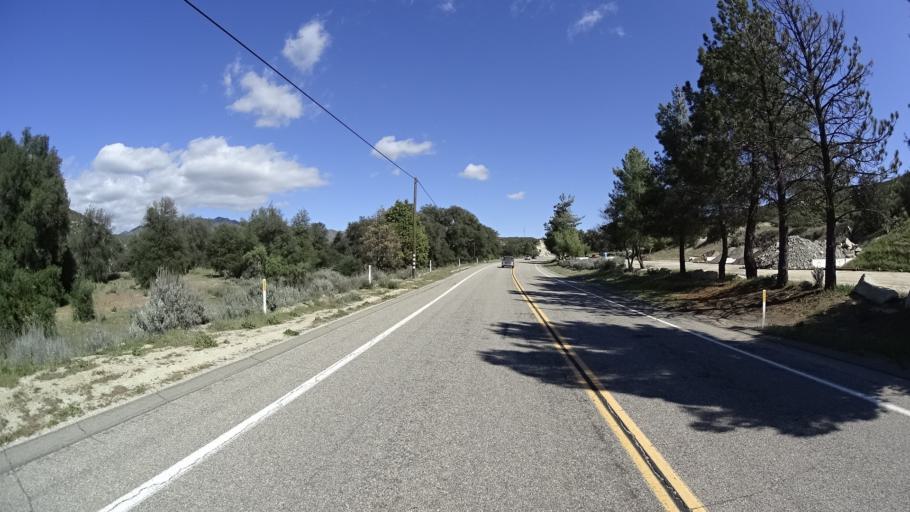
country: US
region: California
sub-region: San Diego County
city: Julian
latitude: 33.2202
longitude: -116.5978
